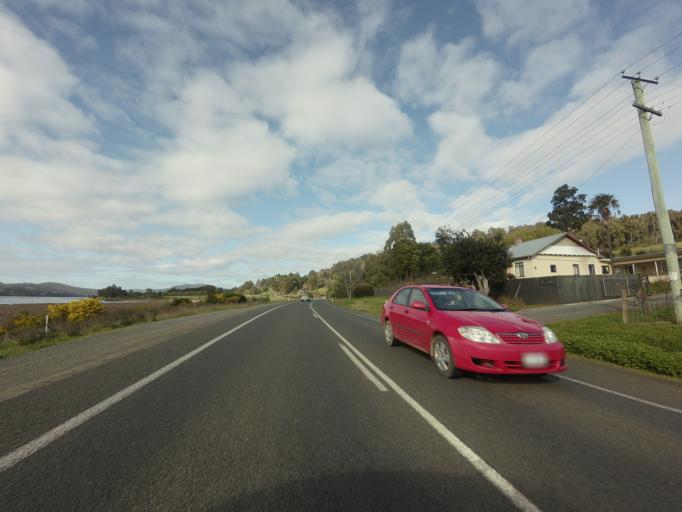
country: AU
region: Tasmania
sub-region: Huon Valley
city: Franklin
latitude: -43.1163
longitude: 146.9929
